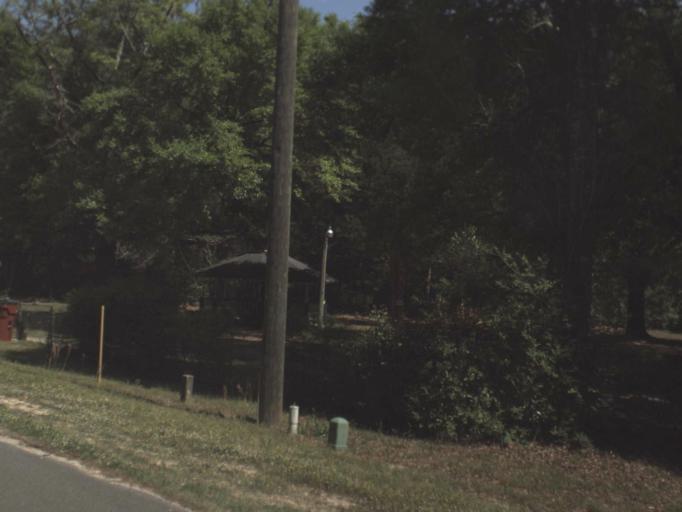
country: US
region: Florida
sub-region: Okaloosa County
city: Crestview
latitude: 30.7126
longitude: -86.7535
